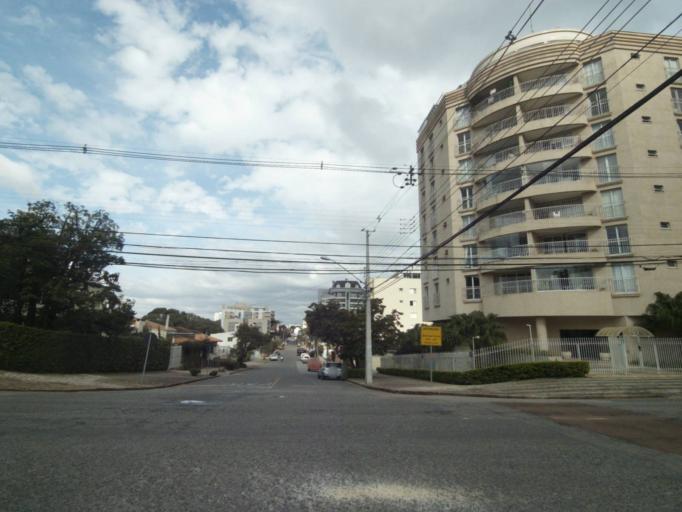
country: BR
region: Parana
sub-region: Curitiba
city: Curitiba
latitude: -25.4051
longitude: -49.2615
